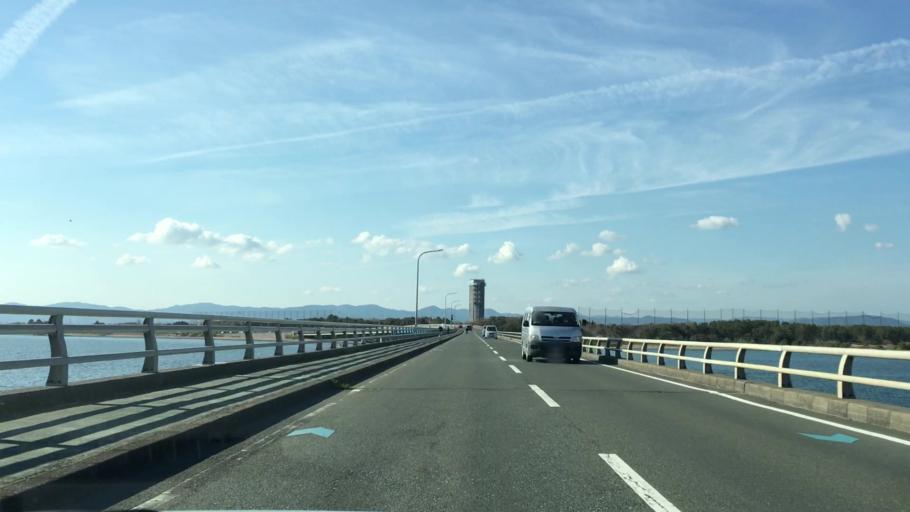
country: JP
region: Shizuoka
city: Kosai-shi
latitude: 34.7093
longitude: 137.6082
